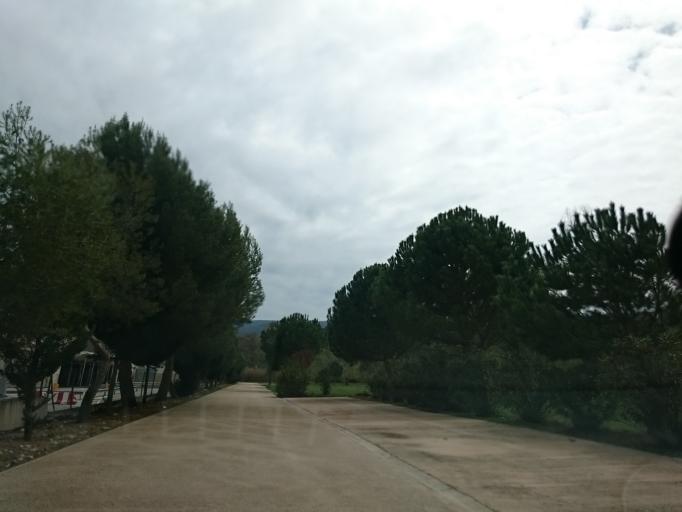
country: ES
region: Catalonia
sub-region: Provincia de Barcelona
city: Sant Sadurni d'Anoia
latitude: 41.4296
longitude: 1.8009
